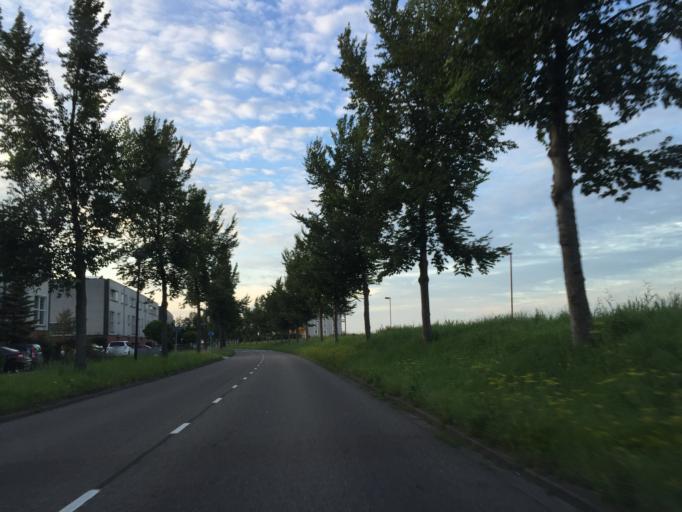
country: NL
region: South Holland
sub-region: Gemeente Rijnwoude
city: Benthuizen
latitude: 52.0729
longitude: 4.5289
